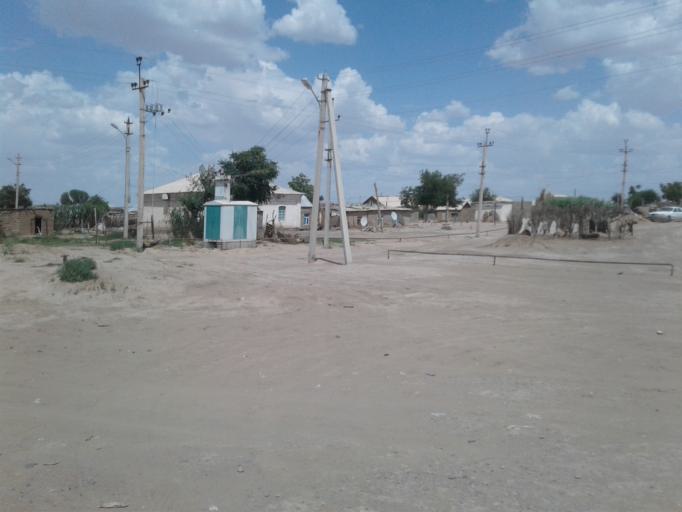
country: TM
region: Ahal
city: Abadan
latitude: 38.7642
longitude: 58.4943
